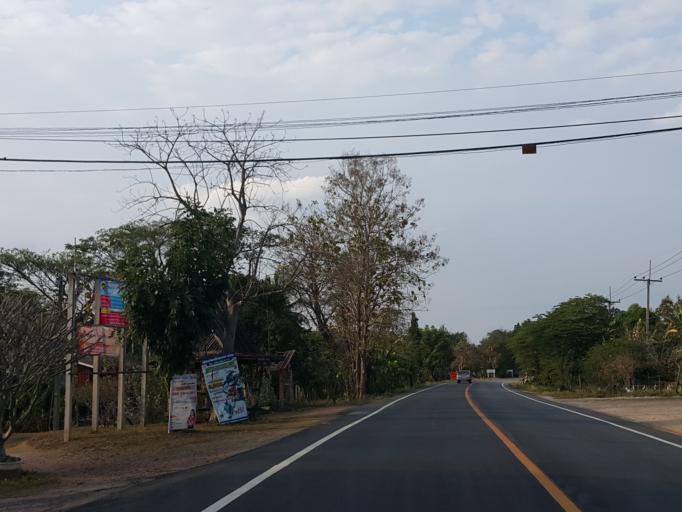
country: TH
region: Lampang
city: Lampang
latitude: 18.4895
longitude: 99.4720
